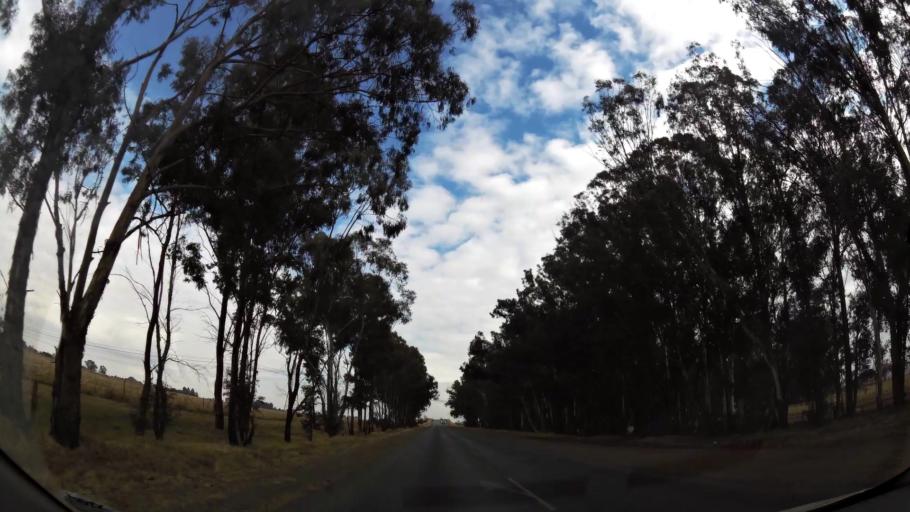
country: ZA
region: Gauteng
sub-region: Sedibeng District Municipality
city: Meyerton
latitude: -26.6317
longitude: 28.0724
